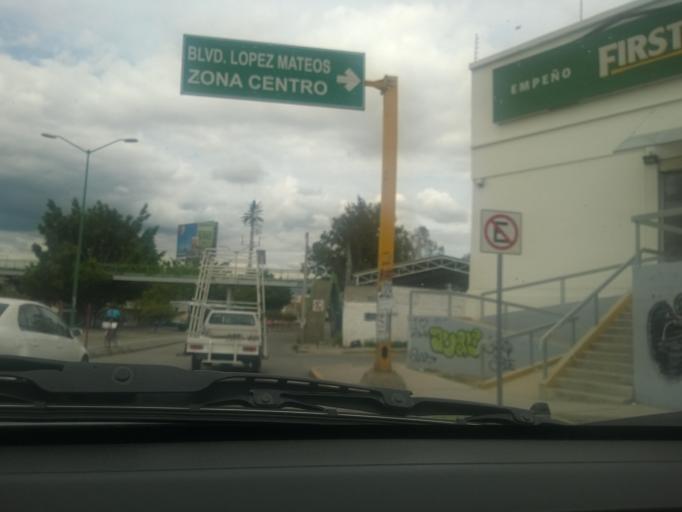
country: MX
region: Guanajuato
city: Leon
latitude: 21.1336
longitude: -101.6983
